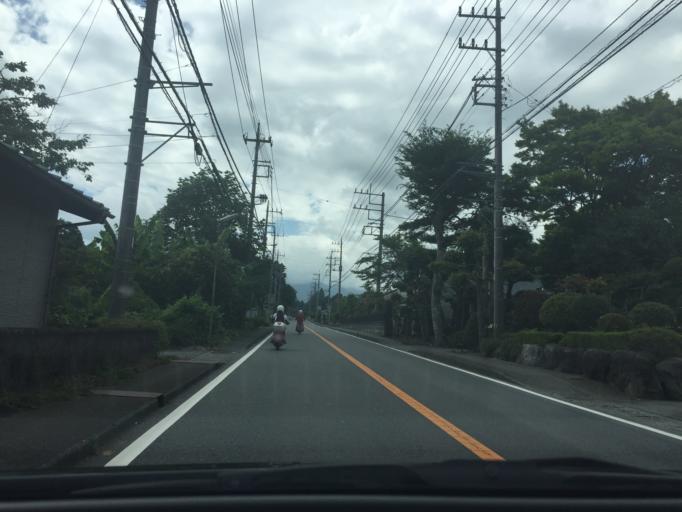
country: JP
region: Shizuoka
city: Gotemba
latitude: 35.2896
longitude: 138.8905
